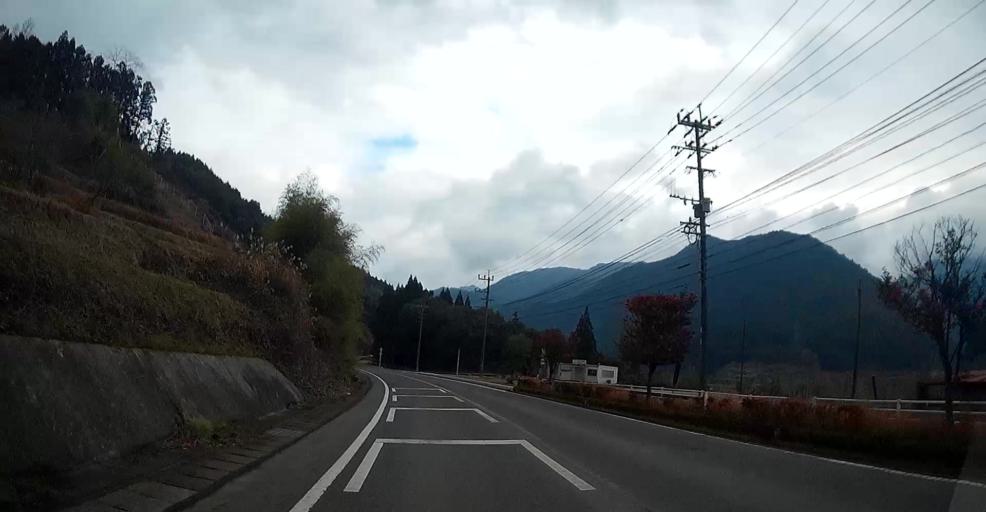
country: JP
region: Kumamoto
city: Matsubase
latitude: 32.6166
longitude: 130.8390
